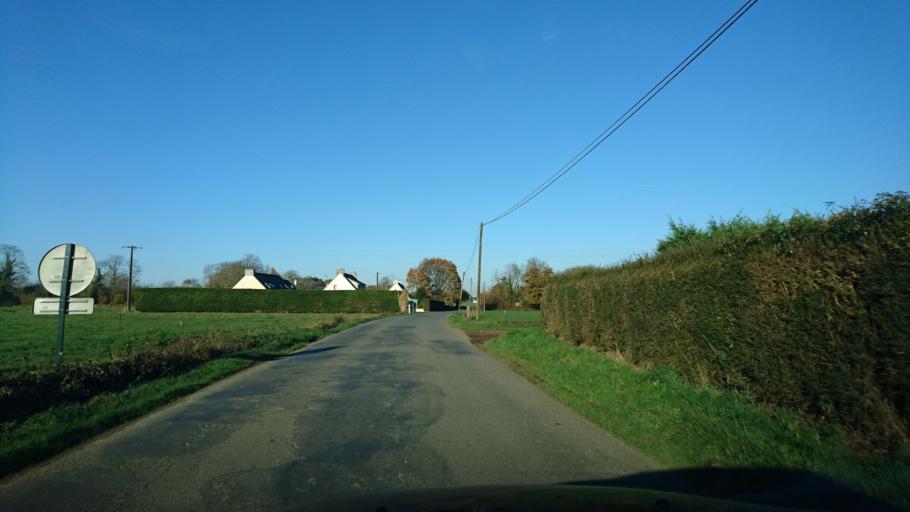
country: FR
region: Brittany
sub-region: Departement des Cotes-d'Armor
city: Pedernec
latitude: 48.5858
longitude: -3.2624
